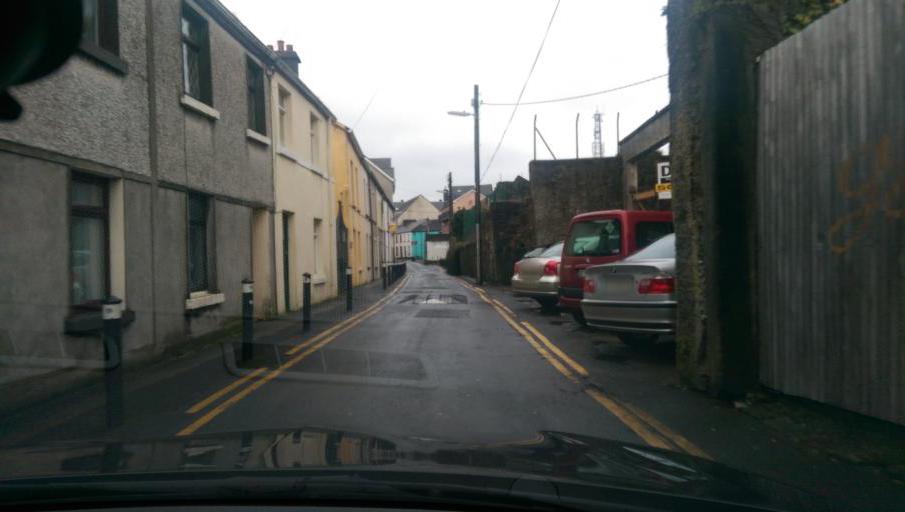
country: IE
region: Connaught
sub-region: County Galway
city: Gaillimh
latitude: 53.2733
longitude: -9.0549
